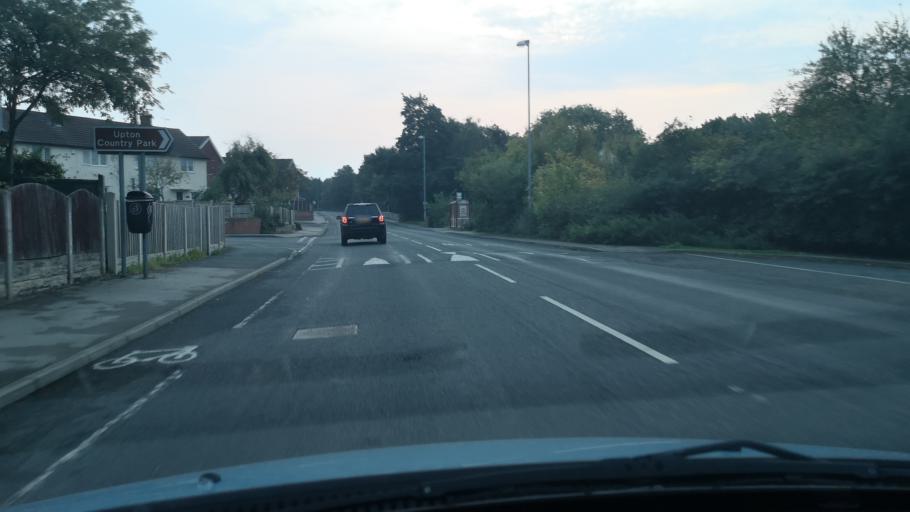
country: GB
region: England
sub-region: City and Borough of Wakefield
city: North Elmsall
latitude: 53.6146
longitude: -1.2802
